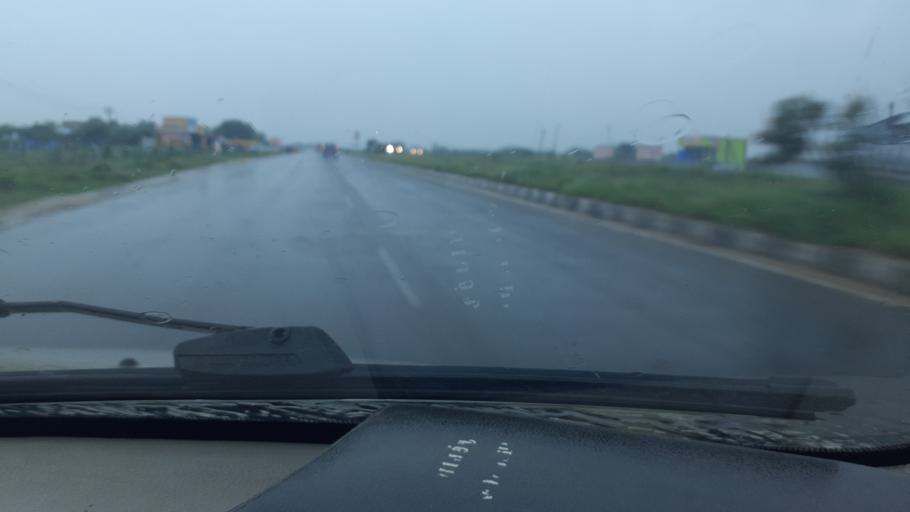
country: IN
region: Tamil Nadu
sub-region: Virudhunagar
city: Sattur
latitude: 9.4186
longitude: 77.9165
